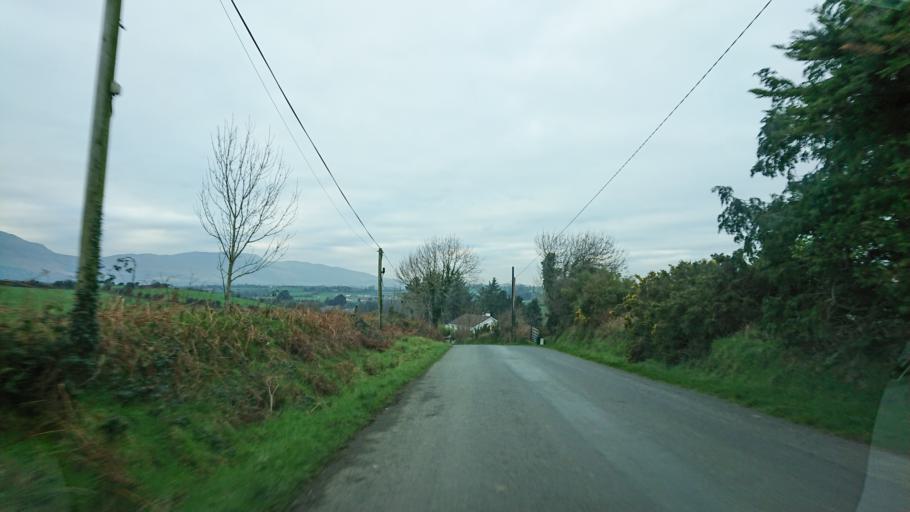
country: IE
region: Munster
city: Carrick-on-Suir
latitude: 52.2772
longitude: -7.4262
